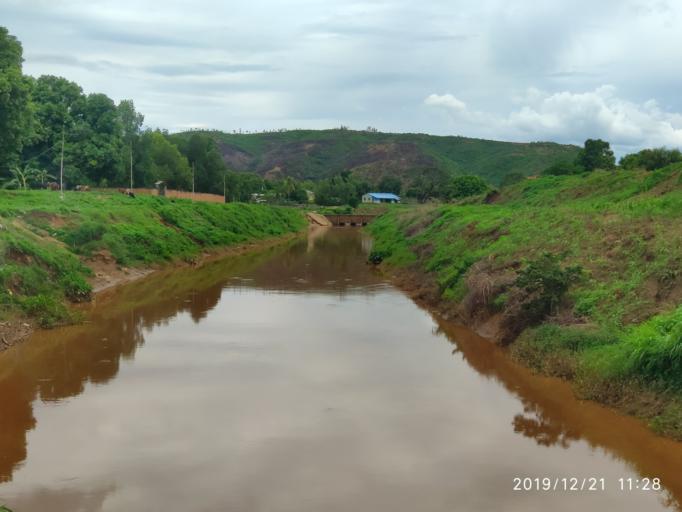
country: MG
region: Diana
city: Ambilobe
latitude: -13.2033
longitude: 49.0467
